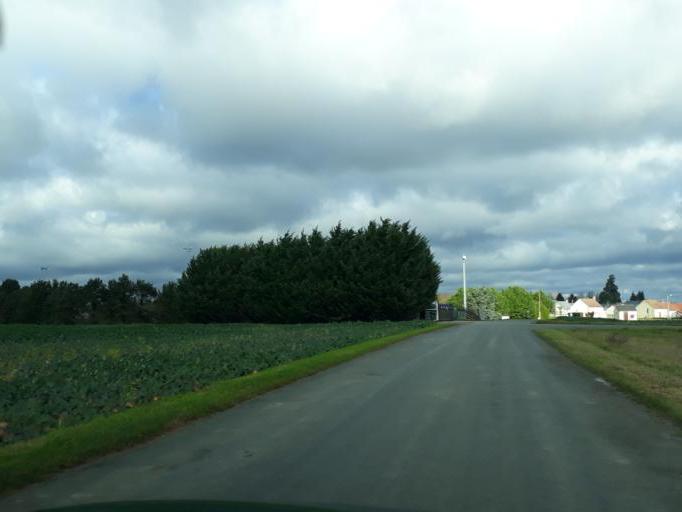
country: FR
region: Centre
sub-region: Departement du Loiret
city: Beaugency
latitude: 47.8234
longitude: 1.5709
